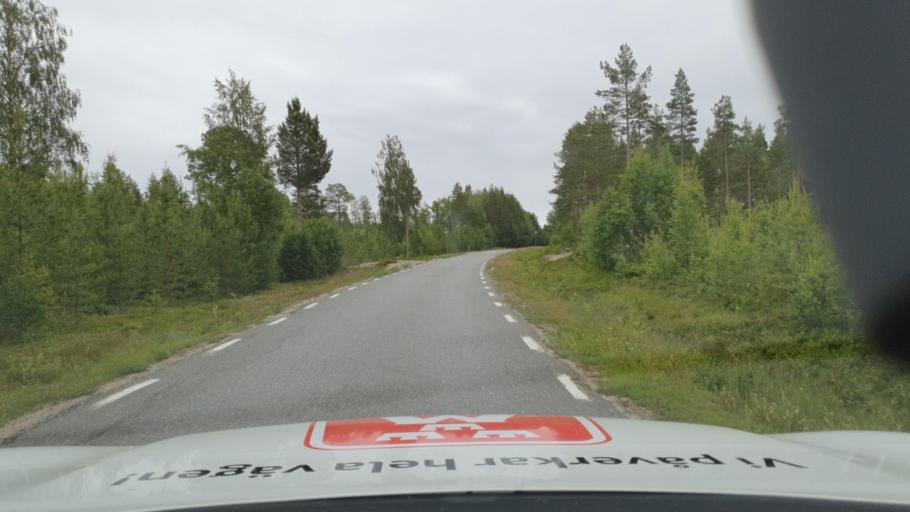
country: SE
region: Vaesterbotten
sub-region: Nordmalings Kommun
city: Nordmaling
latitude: 63.4307
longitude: 19.4914
